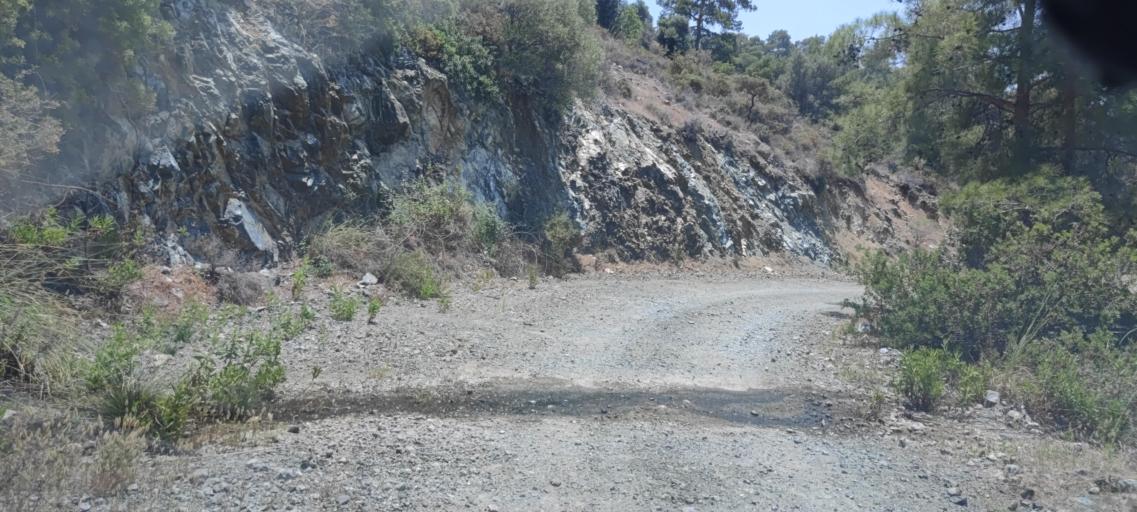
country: CY
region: Limassol
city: Pano Polemidia
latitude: 34.8030
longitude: 33.0282
